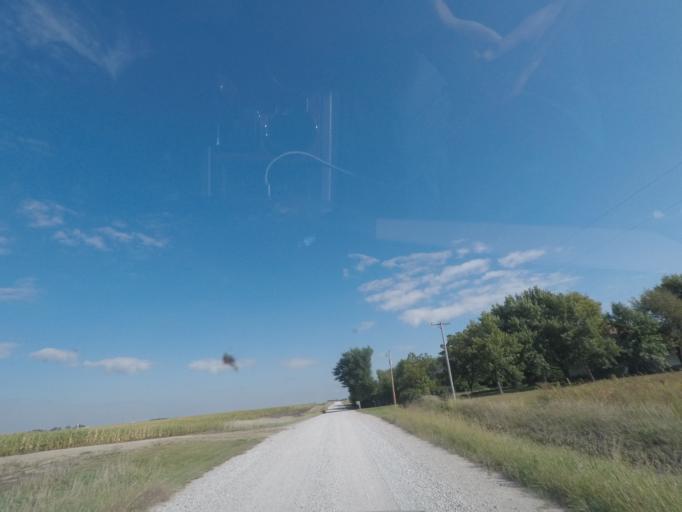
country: US
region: Iowa
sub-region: Story County
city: Nevada
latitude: 42.0356
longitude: -93.4252
